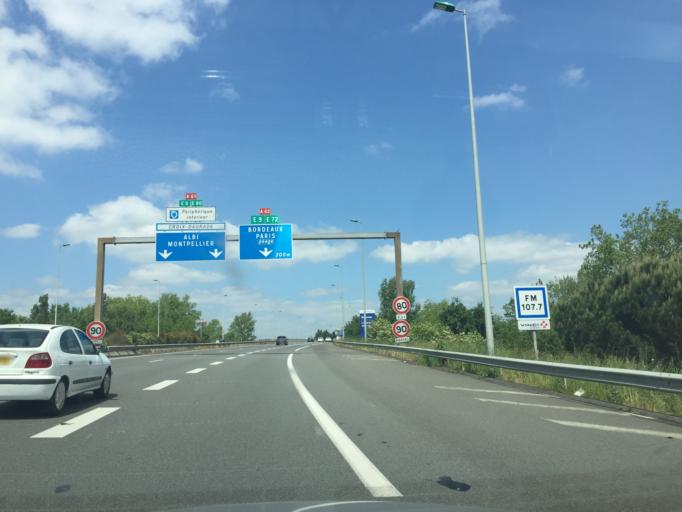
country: FR
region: Midi-Pyrenees
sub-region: Departement de la Haute-Garonne
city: Aucamville
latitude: 43.6504
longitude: 1.4225
